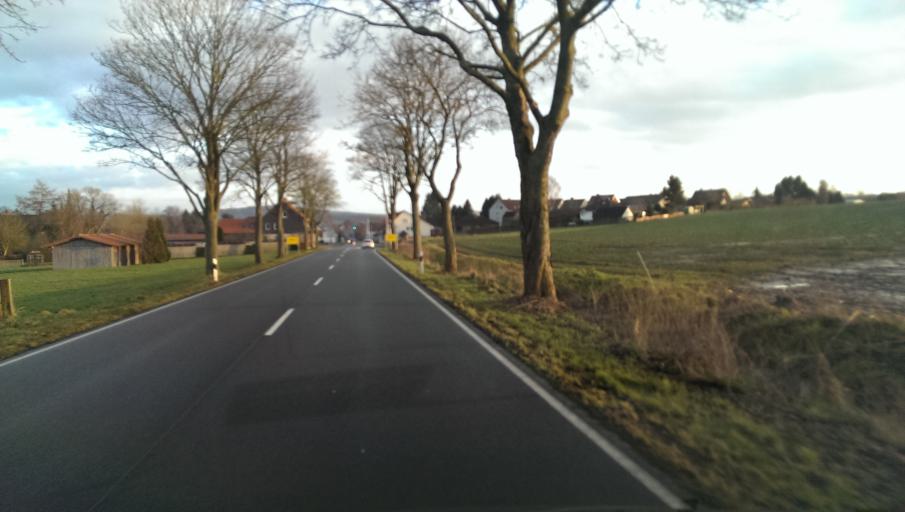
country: DE
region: Lower Saxony
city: Eimen
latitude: 51.8722
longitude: 9.8039
